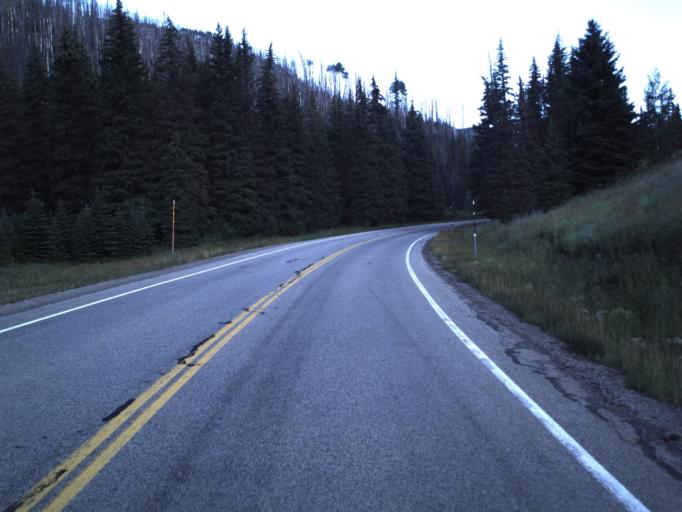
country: US
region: Utah
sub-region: Sanpete County
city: Fairview
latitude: 39.5424
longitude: -111.1627
